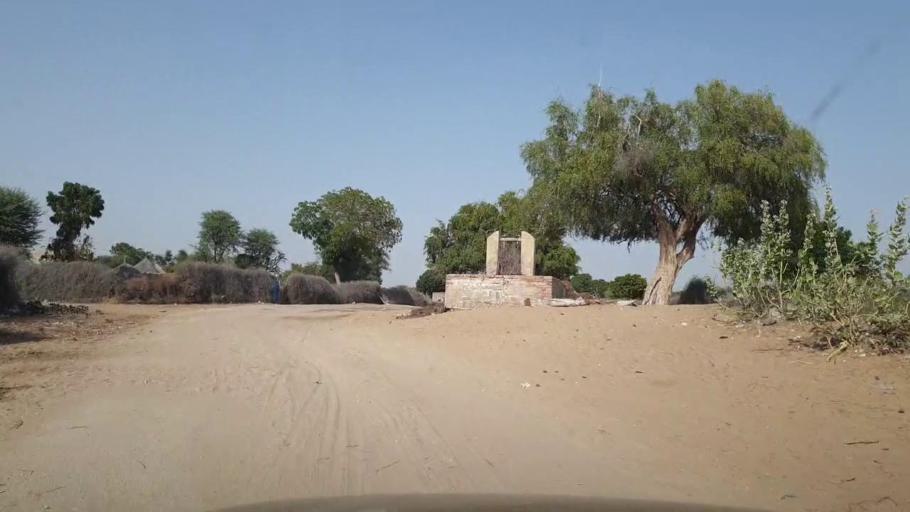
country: PK
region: Sindh
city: Islamkot
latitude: 25.1337
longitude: 70.4590
